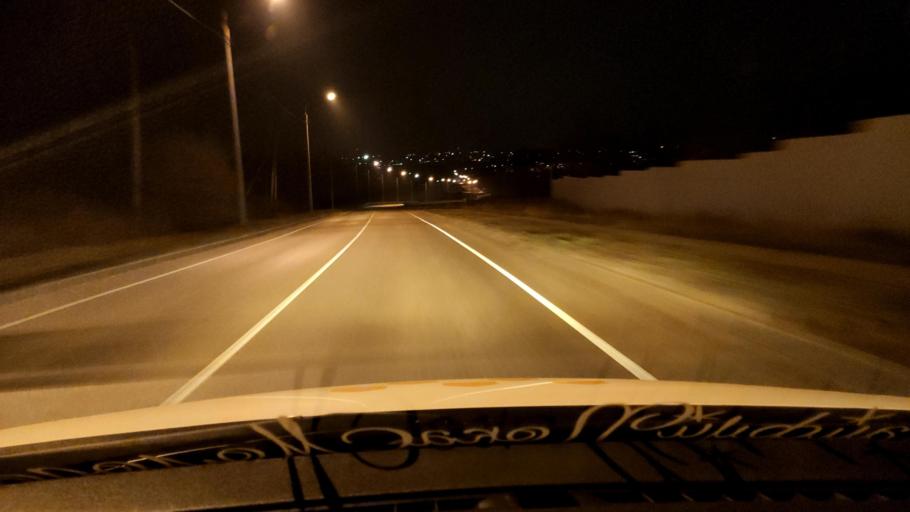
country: RU
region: Voronezj
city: Semiluki
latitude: 51.6699
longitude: 39.0367
